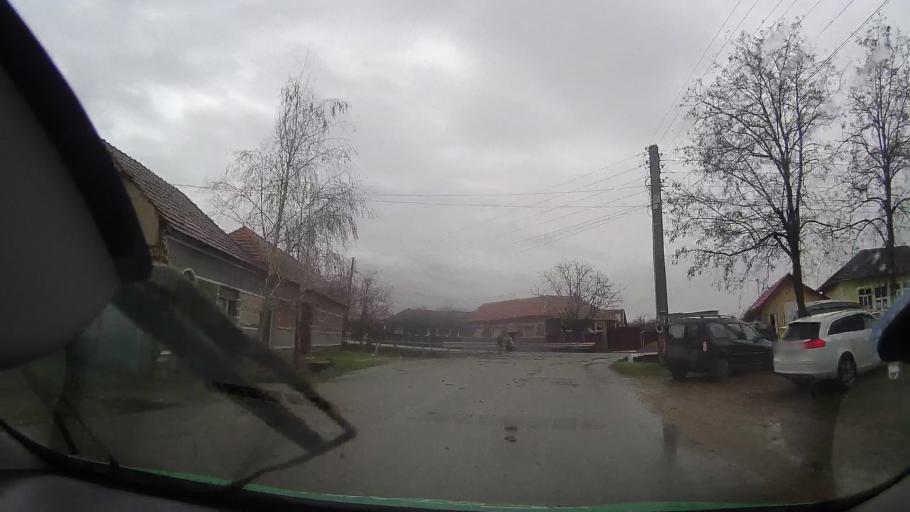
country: RO
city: Capalna
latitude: 46.7089
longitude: 22.0543
